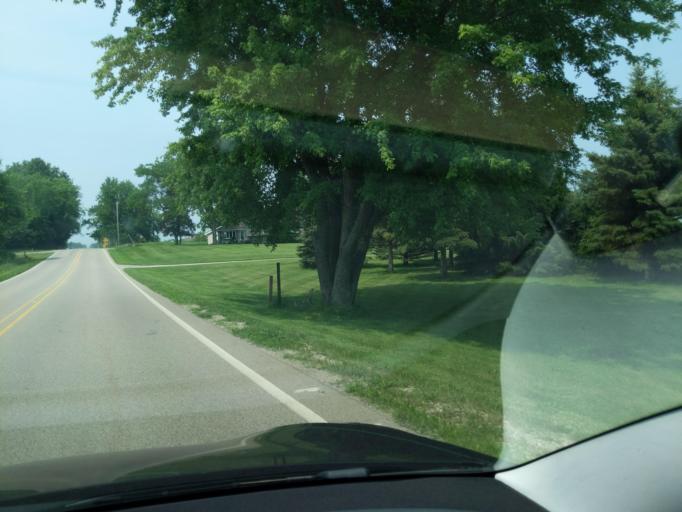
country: US
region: Michigan
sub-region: Clinton County
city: DeWitt
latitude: 42.8103
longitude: -84.5723
